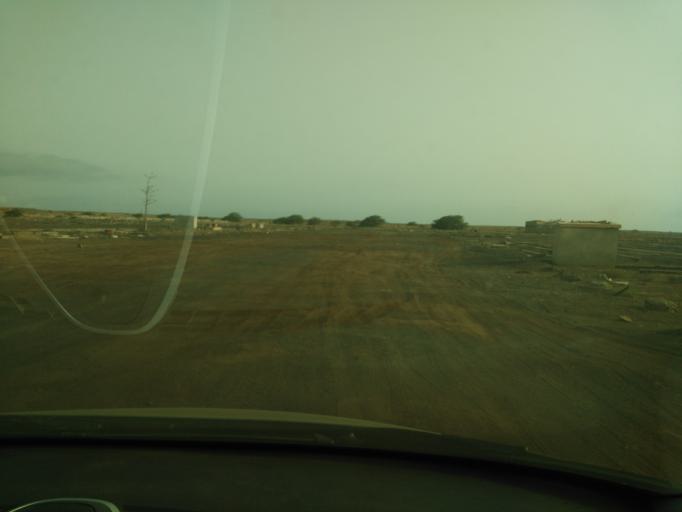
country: CV
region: Sal
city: Santa Maria
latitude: 16.6659
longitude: -22.9331
